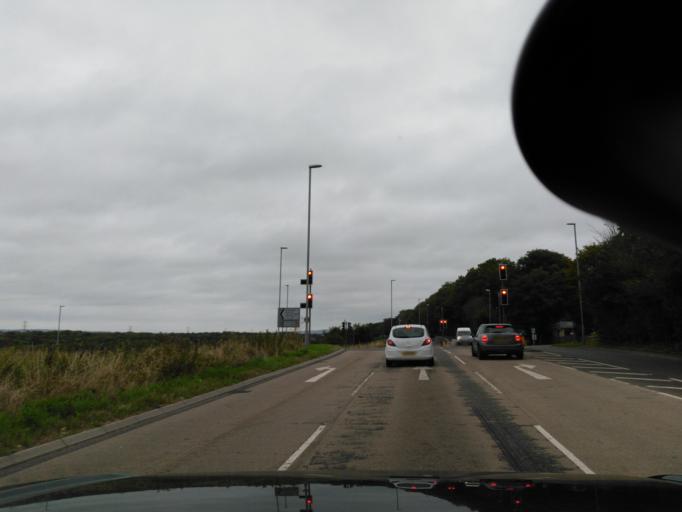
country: GB
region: England
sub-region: Wiltshire
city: North Bradley
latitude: 51.3009
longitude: -2.1784
